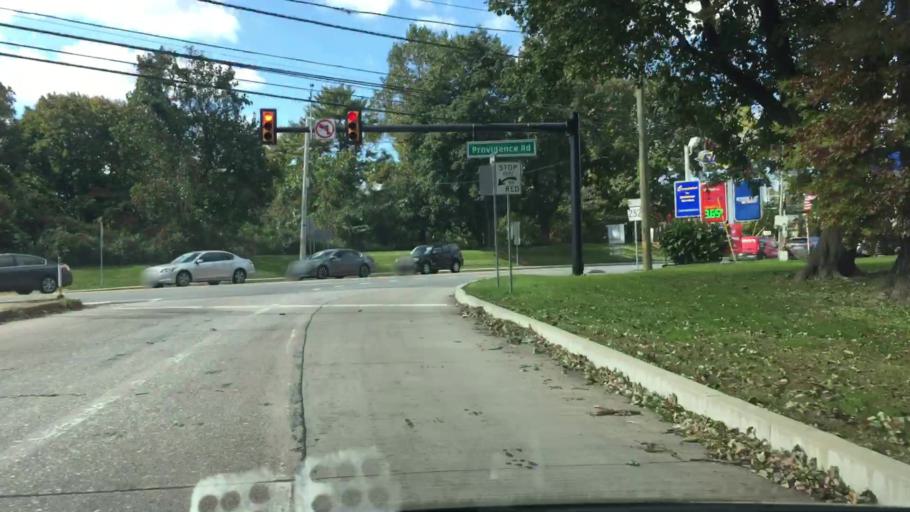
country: US
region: Pennsylvania
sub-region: Delaware County
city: Media
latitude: 39.9365
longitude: -75.3918
